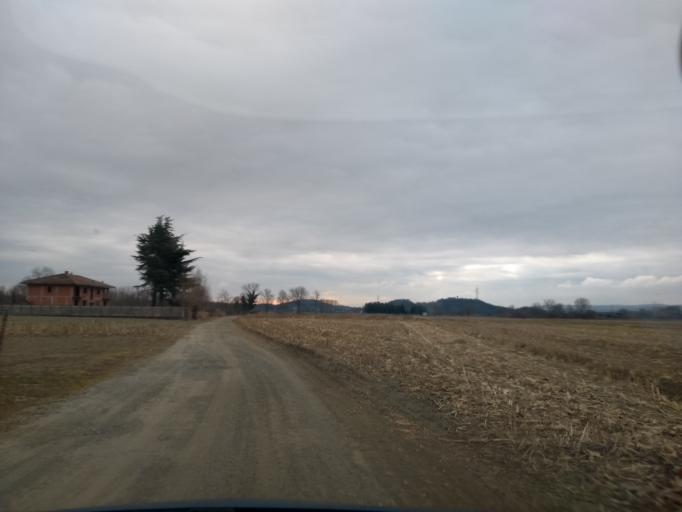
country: IT
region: Piedmont
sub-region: Provincia di Torino
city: Fiorano Canavese
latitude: 45.4823
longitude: 7.8417
